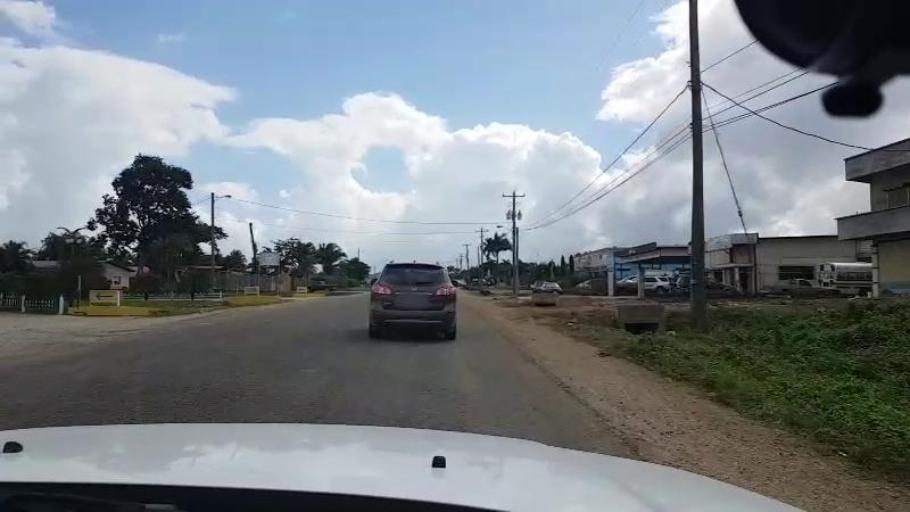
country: BZ
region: Cayo
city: Belmopan
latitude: 17.2454
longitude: -88.7835
